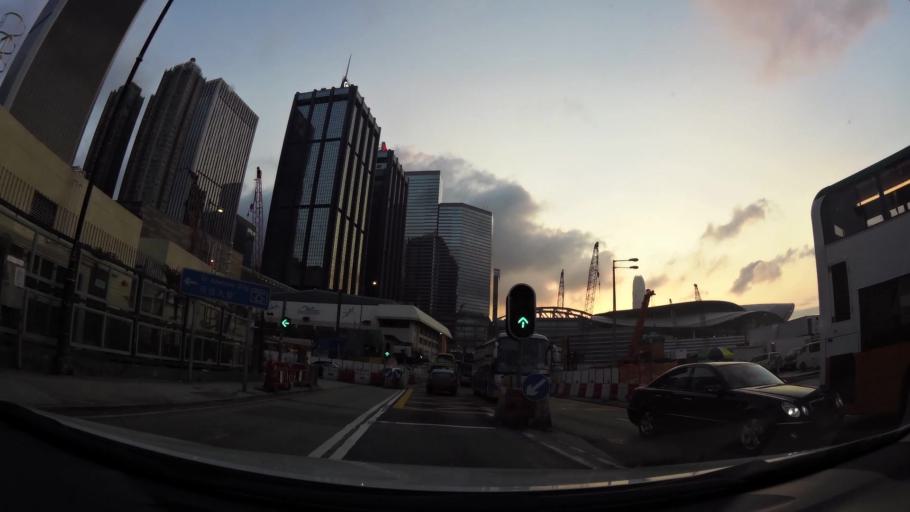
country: HK
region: Wanchai
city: Wan Chai
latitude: 22.2822
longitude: 114.1775
